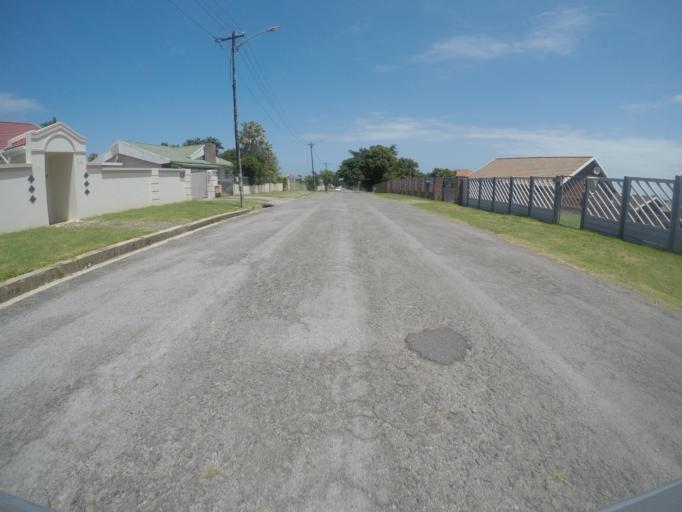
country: ZA
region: Eastern Cape
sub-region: Buffalo City Metropolitan Municipality
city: East London
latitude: -32.9734
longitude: 27.8802
